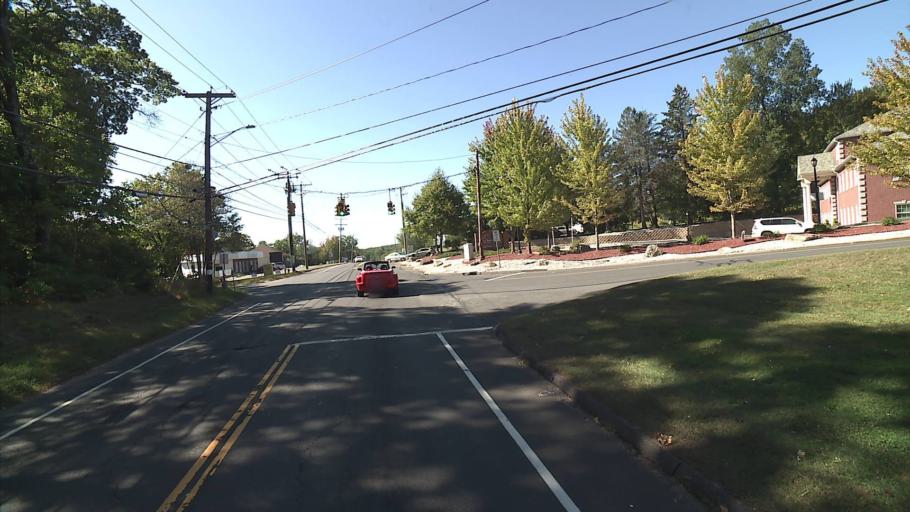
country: US
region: Connecticut
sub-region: New Haven County
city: Wolcott
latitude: 41.5930
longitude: -72.9887
